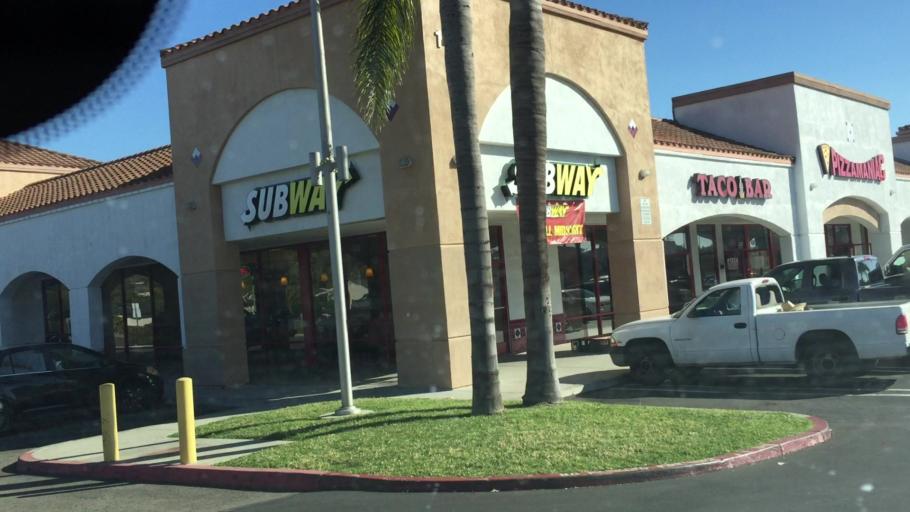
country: US
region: California
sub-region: San Diego County
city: Vista
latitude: 33.2211
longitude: -117.2437
